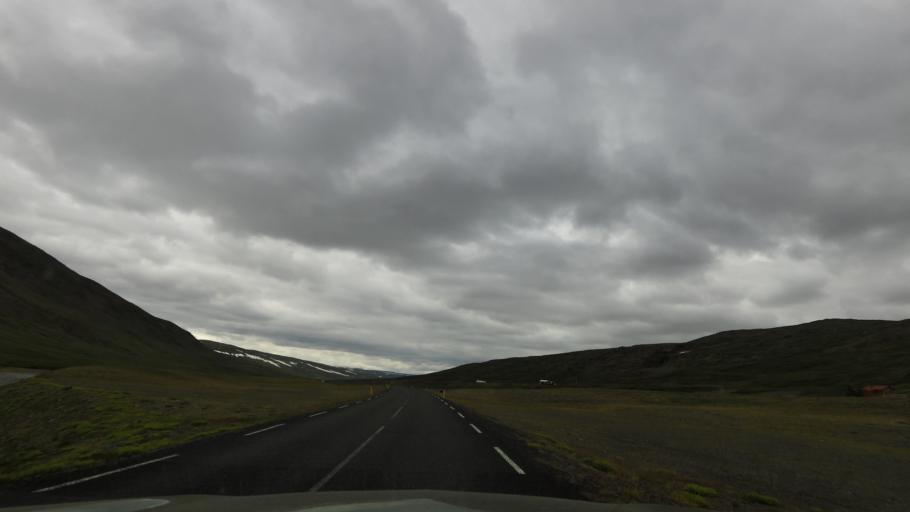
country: IS
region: West
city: Stykkisholmur
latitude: 65.7452
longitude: -21.9330
